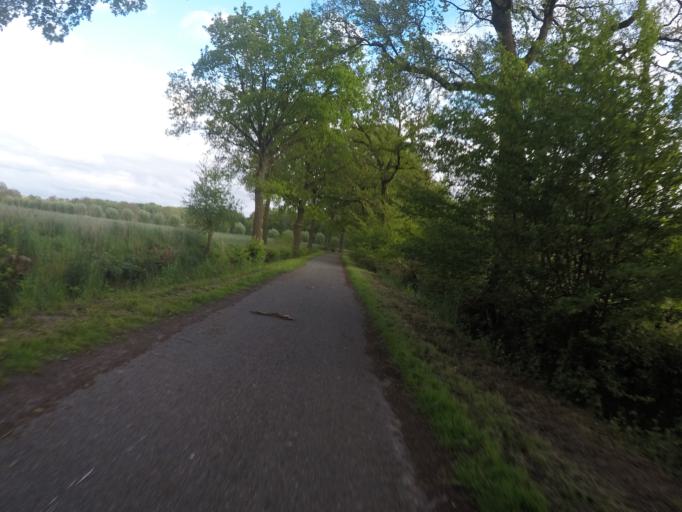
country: DE
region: Schleswig-Holstein
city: Bonningstedt
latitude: 53.6799
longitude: 9.9292
